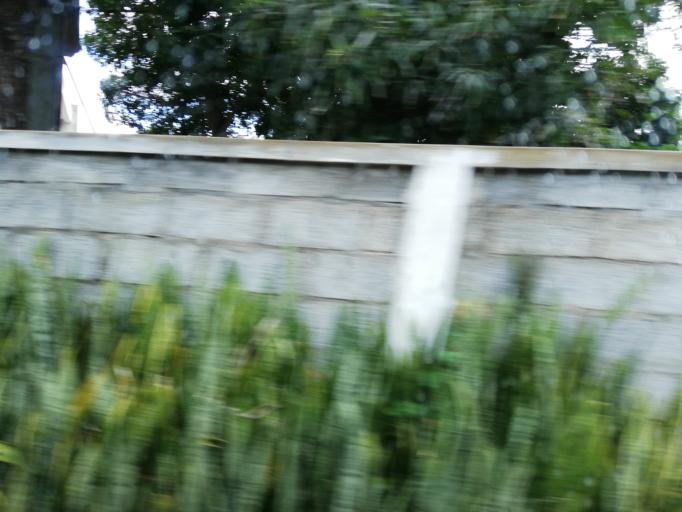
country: MU
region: Moka
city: Moka
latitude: -20.2177
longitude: 57.4728
